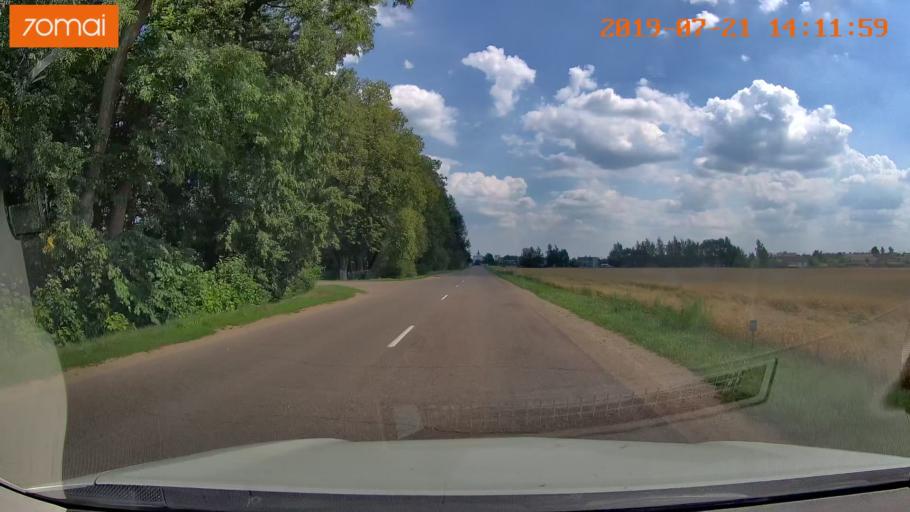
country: BY
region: Grodnenskaya
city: Karelichy
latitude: 53.6543
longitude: 26.1623
